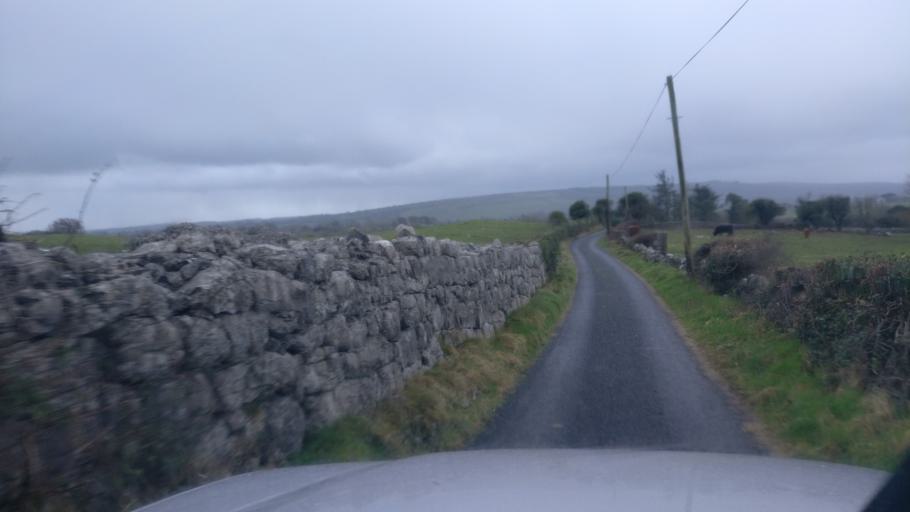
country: IE
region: Connaught
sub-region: County Galway
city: Loughrea
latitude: 53.1937
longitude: -8.6810
